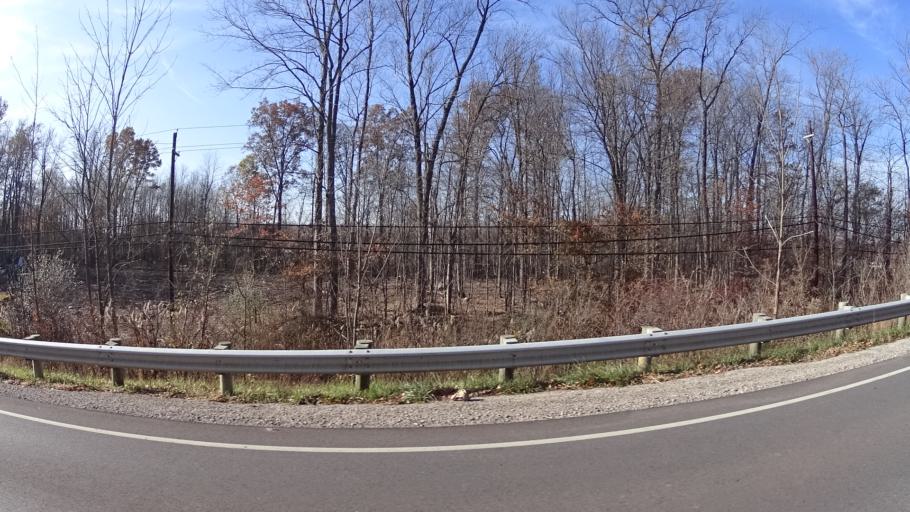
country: US
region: Ohio
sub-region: Lorain County
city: Avon Center
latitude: 41.4631
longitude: -81.9998
